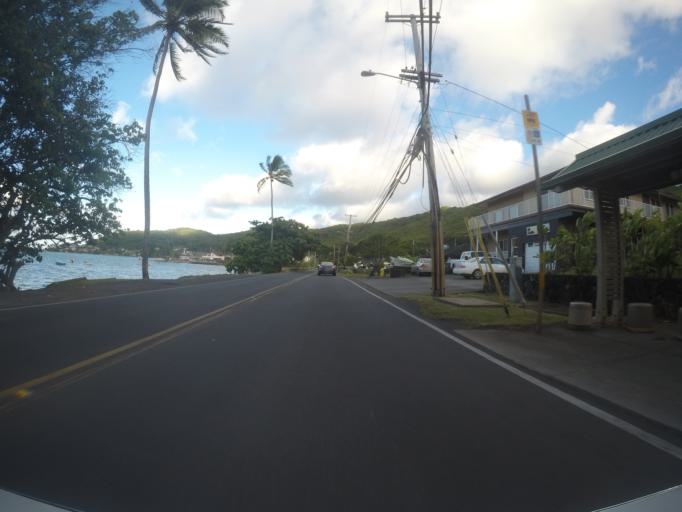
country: US
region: Hawaii
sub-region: Honolulu County
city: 'Ahuimanu
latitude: 21.4542
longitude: -157.8262
